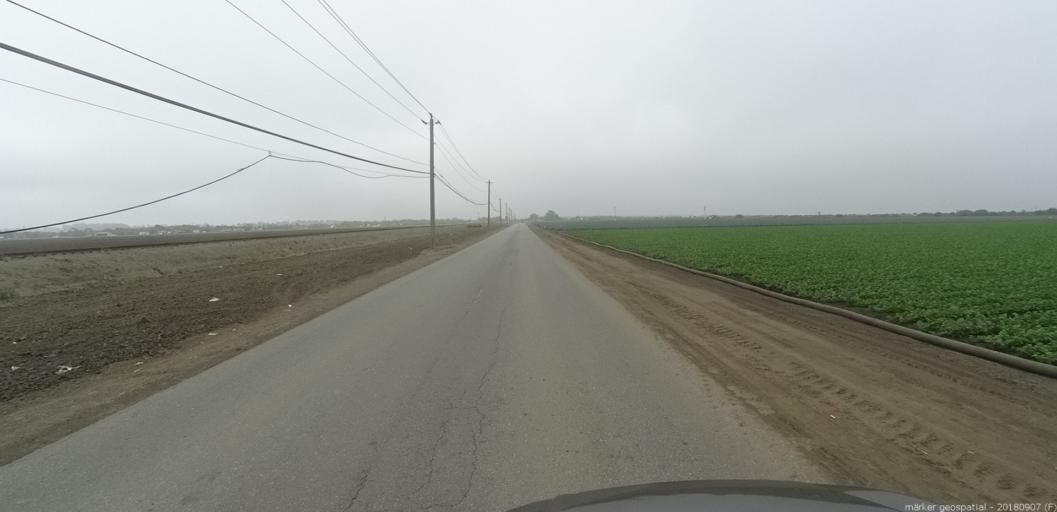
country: US
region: California
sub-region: Monterey County
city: Castroville
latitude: 36.7395
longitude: -121.7694
